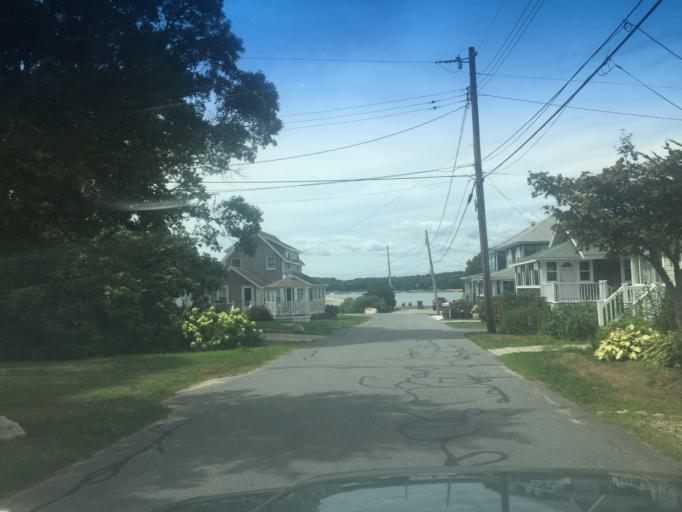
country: US
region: Massachusetts
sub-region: Barnstable County
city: Pocasset
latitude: 41.6856
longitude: -70.6277
